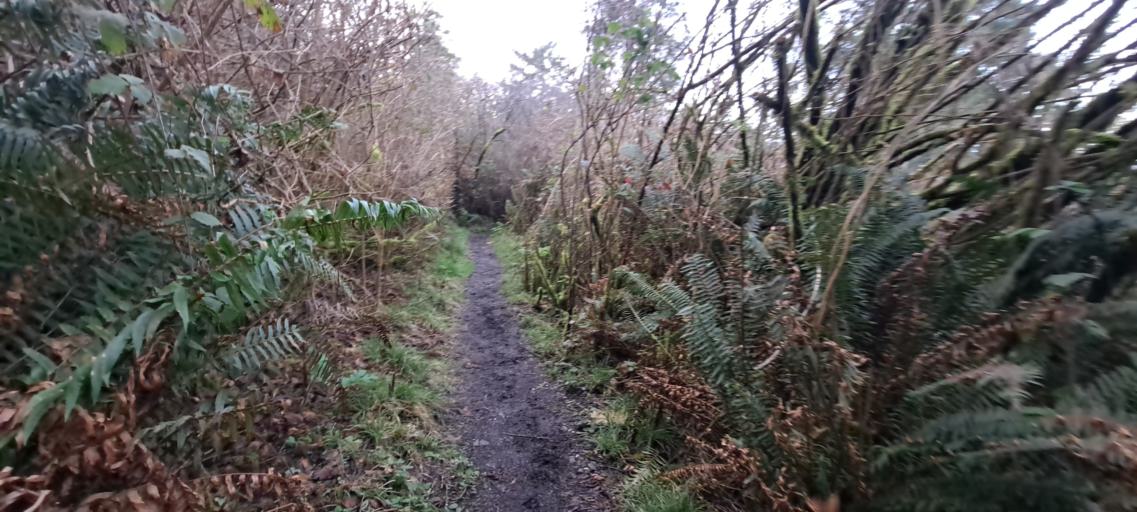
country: US
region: California
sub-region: Humboldt County
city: Ferndale
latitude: 40.5721
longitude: -124.2583
